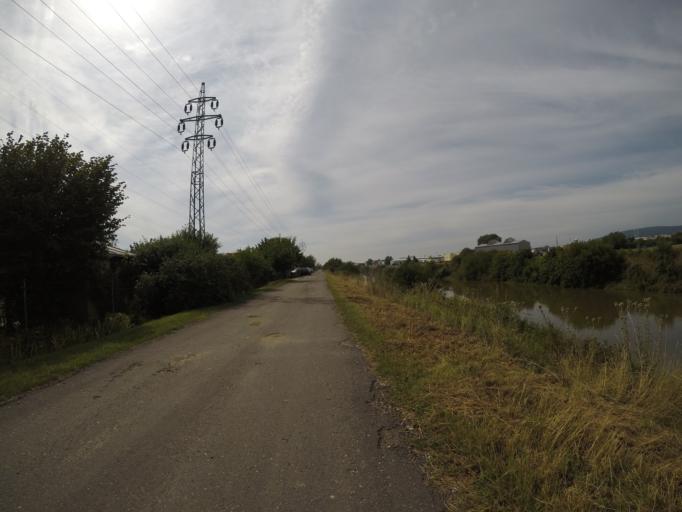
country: SK
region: Trenciansky
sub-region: Okres Nove Mesto nad Vahom
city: Nove Mesto nad Vahom
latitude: 48.7541
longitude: 17.8469
